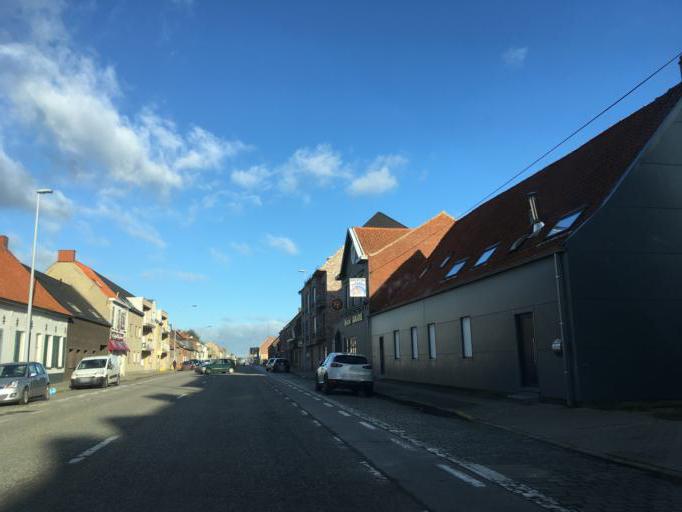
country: BE
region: Flanders
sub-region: Provincie West-Vlaanderen
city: Ingelmunster
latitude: 50.9255
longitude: 3.2537
